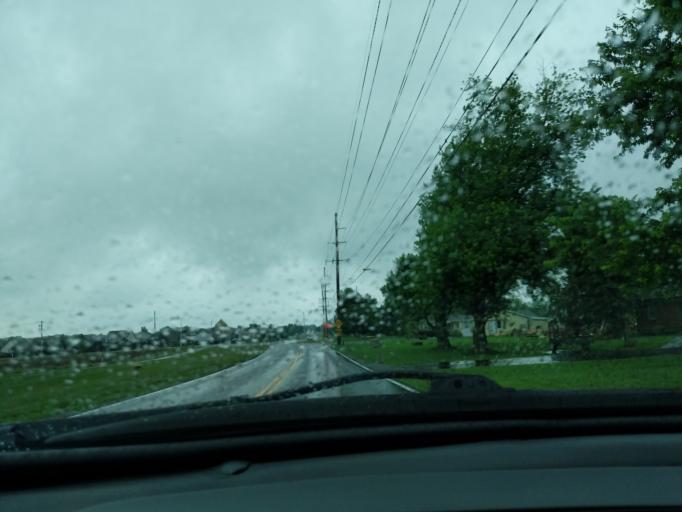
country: US
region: Indiana
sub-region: Hamilton County
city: Noblesville
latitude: 40.0741
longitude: -86.0334
